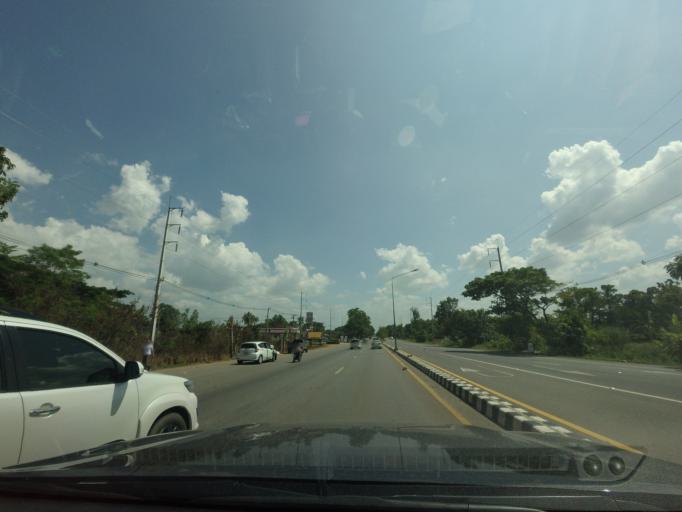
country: TH
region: Phetchabun
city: Nong Phai
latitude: 16.0688
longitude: 101.0694
